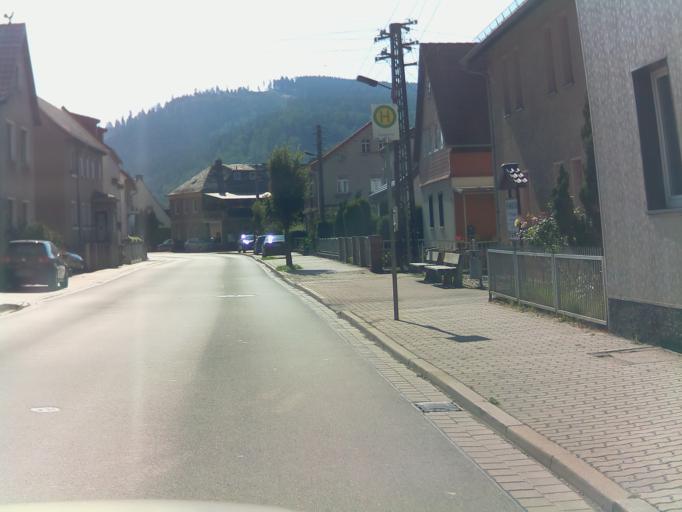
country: DE
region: Thuringia
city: Kaulsdorf
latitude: 50.6212
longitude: 11.4299
